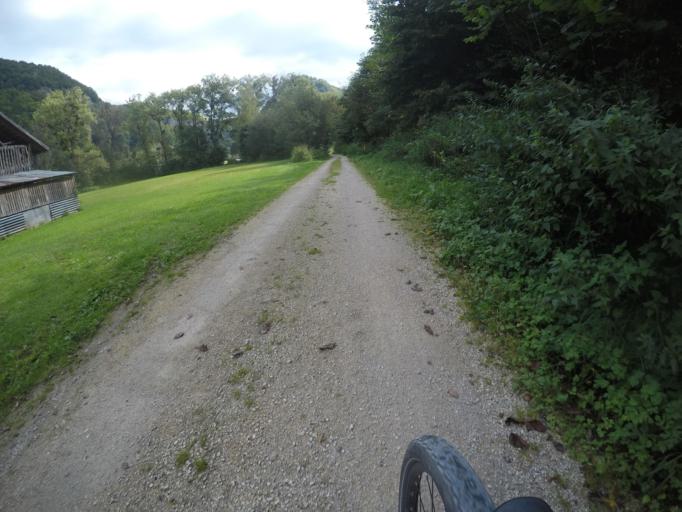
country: DE
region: Baden-Wuerttemberg
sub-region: Tuebingen Region
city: Bad Urach
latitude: 48.4716
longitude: 9.4142
